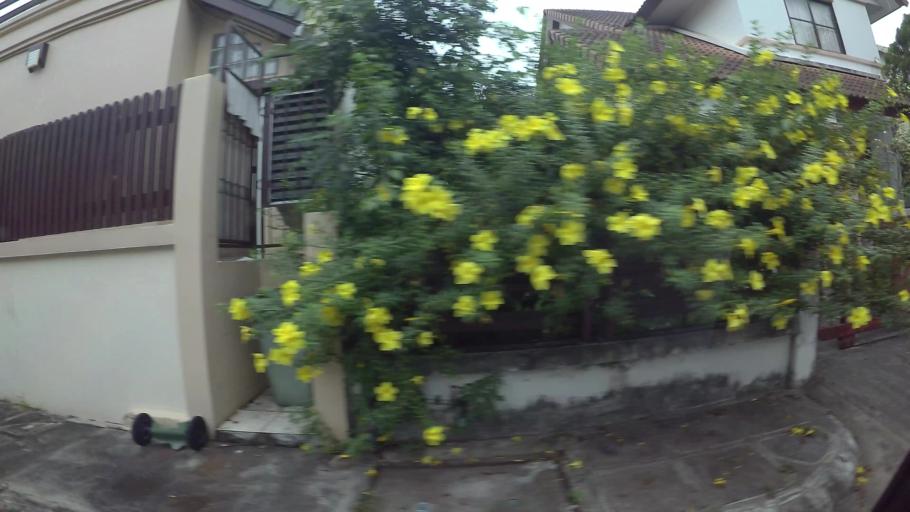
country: TH
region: Chon Buri
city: Si Racha
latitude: 13.1518
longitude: 100.9806
